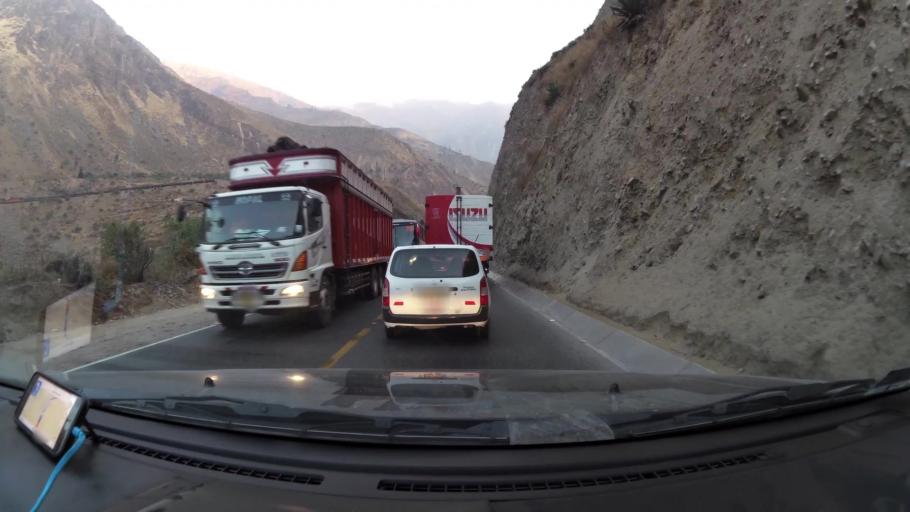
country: PE
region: Lima
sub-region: Provincia de Huarochiri
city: Surco
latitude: -11.8689
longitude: -76.4259
